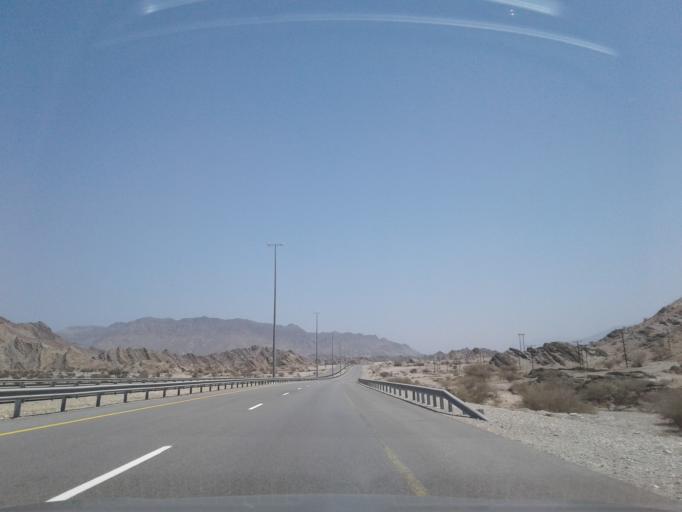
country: OM
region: Muhafazat Masqat
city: Muscat
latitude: 23.3500
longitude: 58.6896
